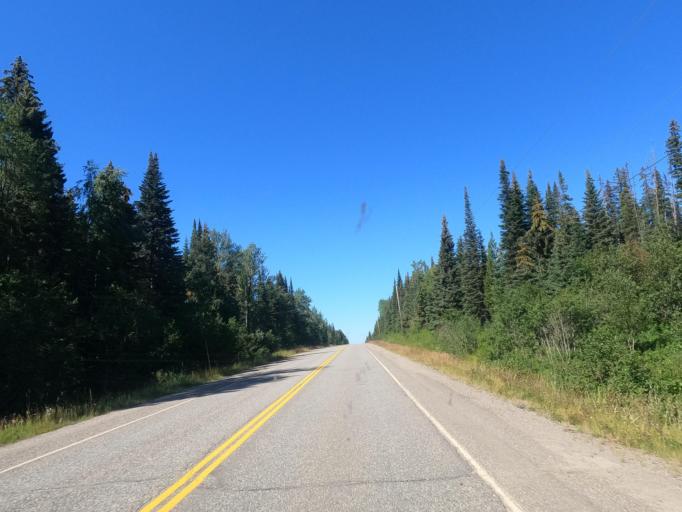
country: CA
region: British Columbia
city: Quesnel
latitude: 53.0285
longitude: -122.0344
